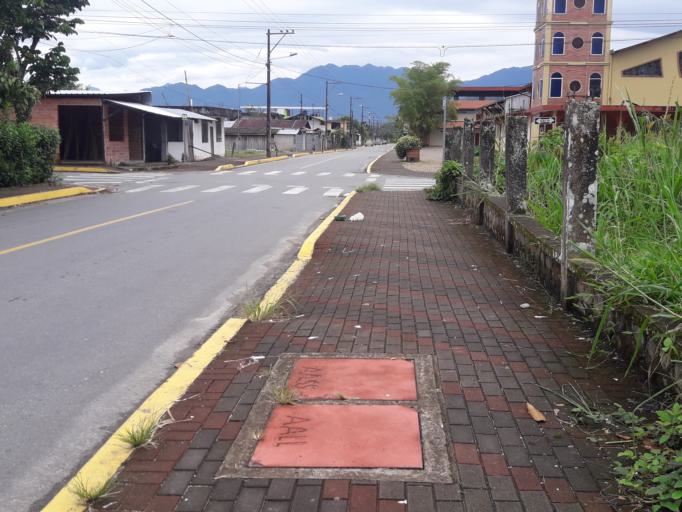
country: EC
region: Napo
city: Tena
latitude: -1.0061
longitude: -77.8140
